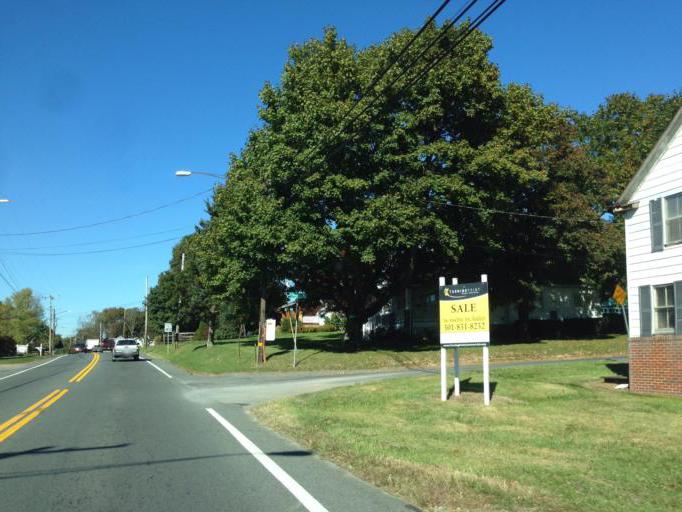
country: US
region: Maryland
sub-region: Montgomery County
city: Damascus
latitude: 39.3077
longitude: -77.1976
